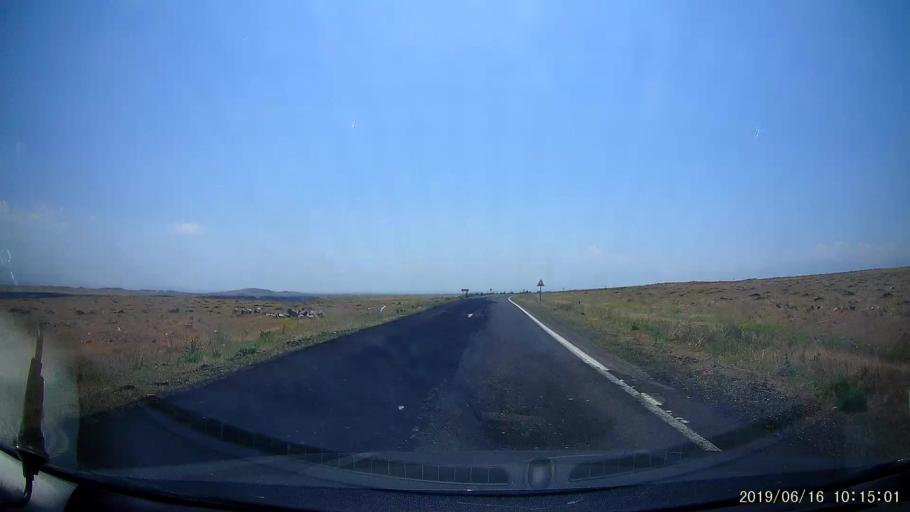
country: TR
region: Igdir
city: Tuzluca
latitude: 40.1799
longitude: 43.6744
